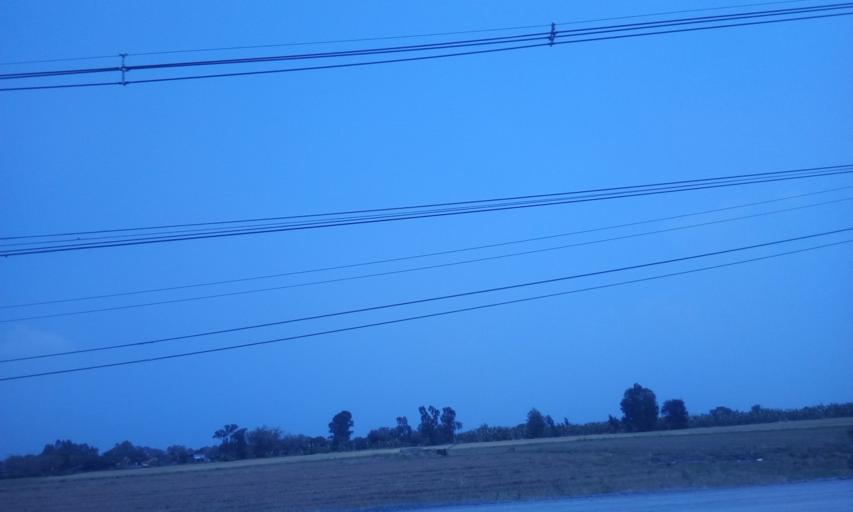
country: TH
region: Chon Buri
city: Phan Thong
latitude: 13.5378
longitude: 101.1480
